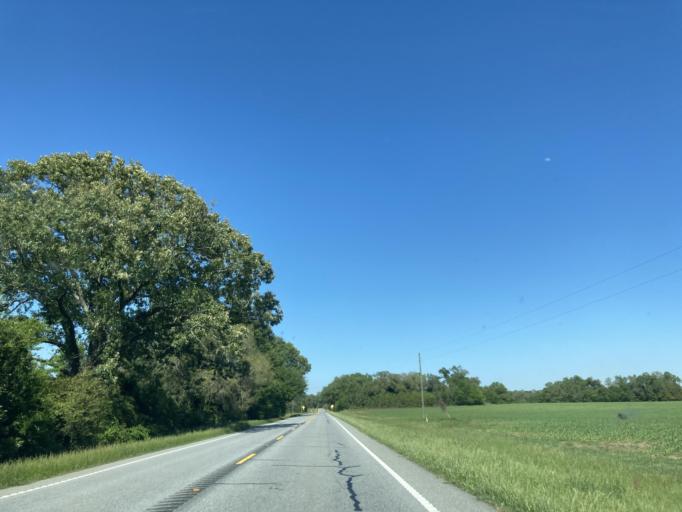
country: US
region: Georgia
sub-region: Baker County
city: Newton
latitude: 31.2001
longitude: -84.5035
